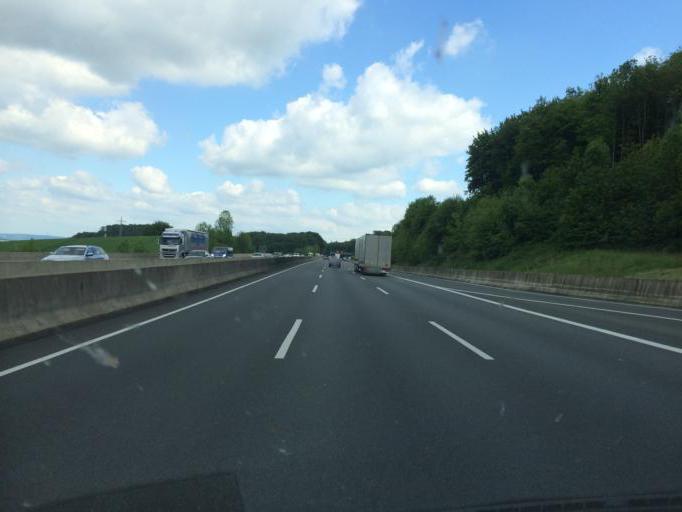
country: DE
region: Lower Saxony
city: Buchholz
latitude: 52.2158
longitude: 9.1701
